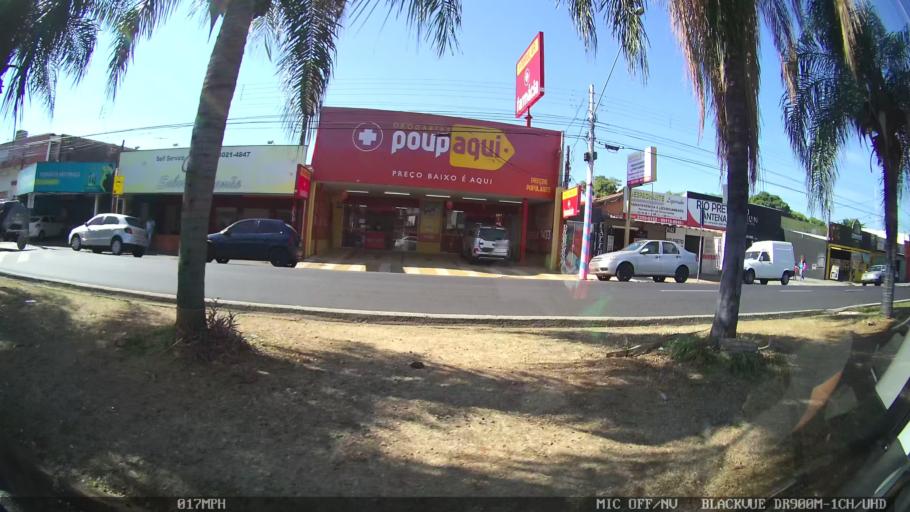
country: BR
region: Sao Paulo
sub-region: Sao Jose Do Rio Preto
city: Sao Jose do Rio Preto
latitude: -20.7793
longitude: -49.3674
